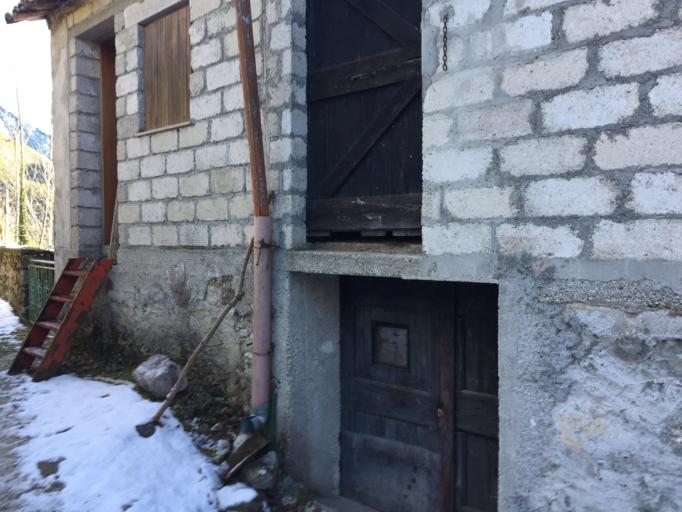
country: IT
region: Friuli Venezia Giulia
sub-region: Provincia di Udine
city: Moggio di Sotto
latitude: 46.4175
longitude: 13.1534
